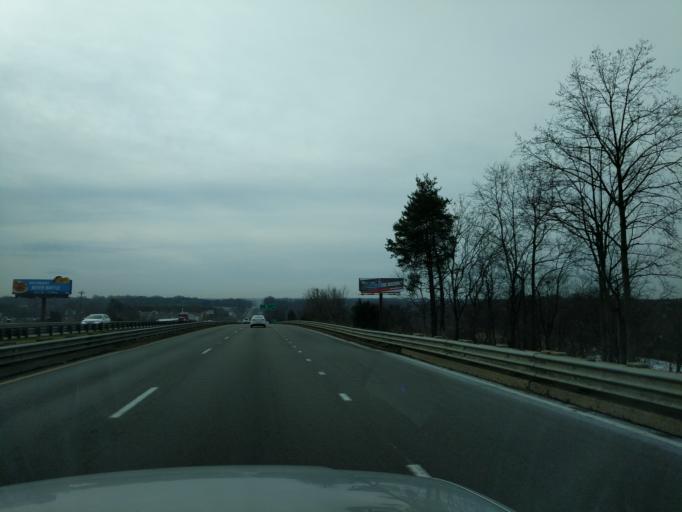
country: US
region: North Carolina
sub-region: Iredell County
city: Statesville
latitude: 35.7741
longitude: -80.8634
